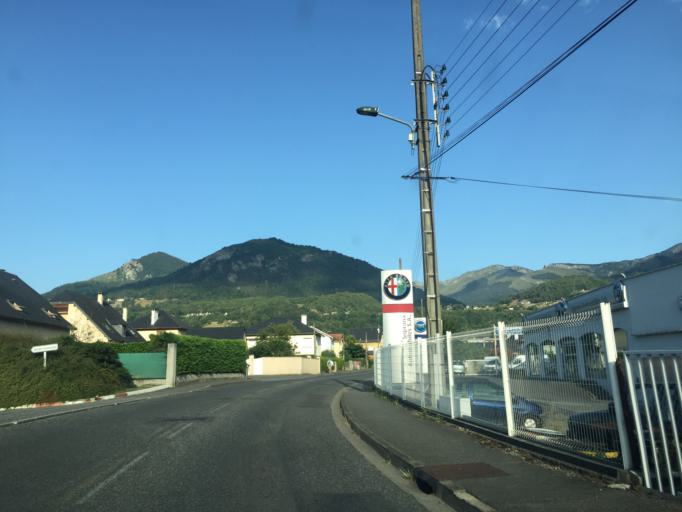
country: FR
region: Midi-Pyrenees
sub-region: Departement des Hautes-Pyrenees
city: Argeles-Gazost
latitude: 43.0056
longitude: -0.0876
